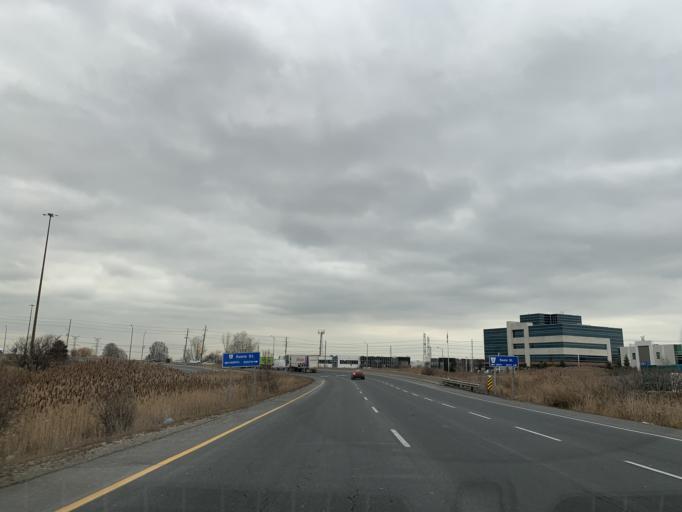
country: CA
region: Ontario
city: Concord
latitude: 43.7911
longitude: -79.4998
